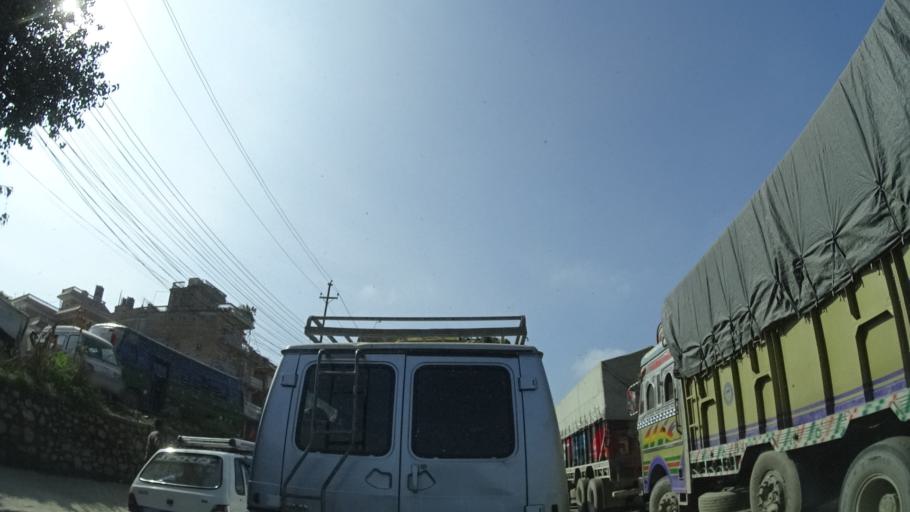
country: NP
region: Central Region
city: Kirtipur
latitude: 27.6980
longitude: 85.2815
